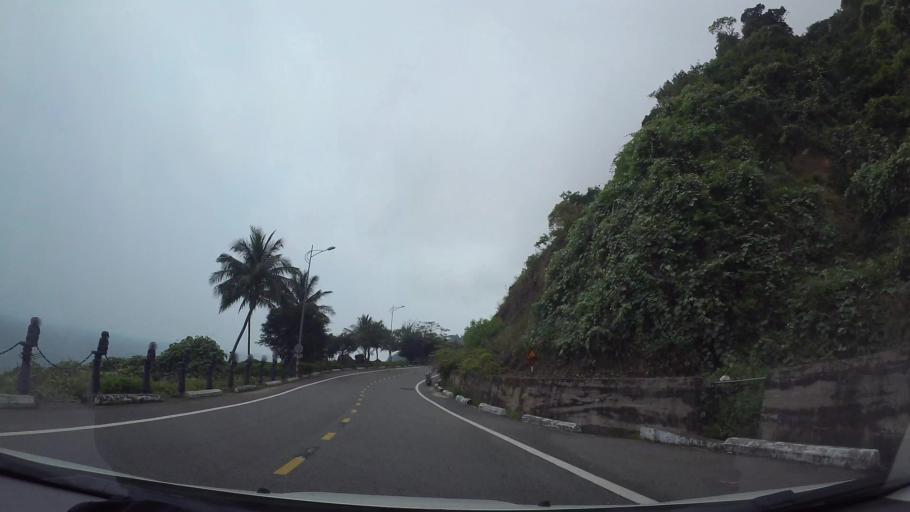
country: VN
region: Da Nang
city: Son Tra
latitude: 16.1099
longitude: 108.3084
